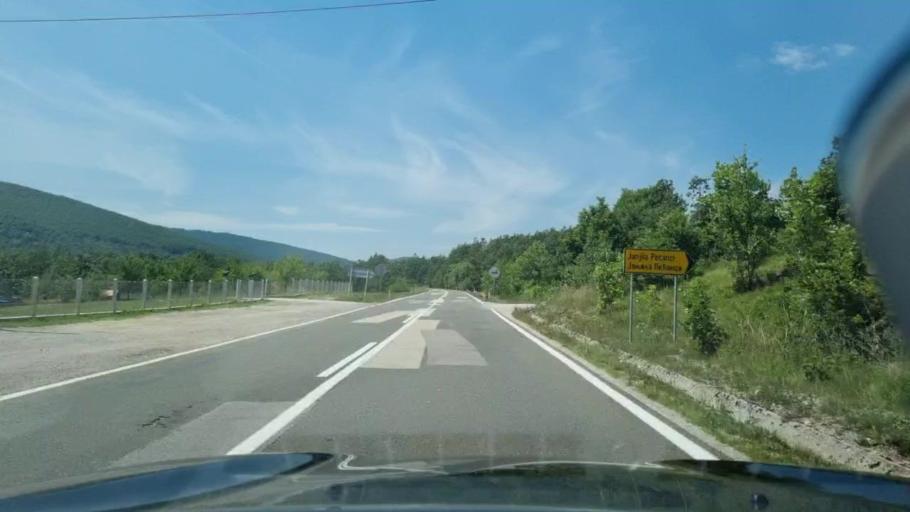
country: BA
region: Federation of Bosnia and Herzegovina
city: Sanica
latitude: 44.5556
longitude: 16.5304
